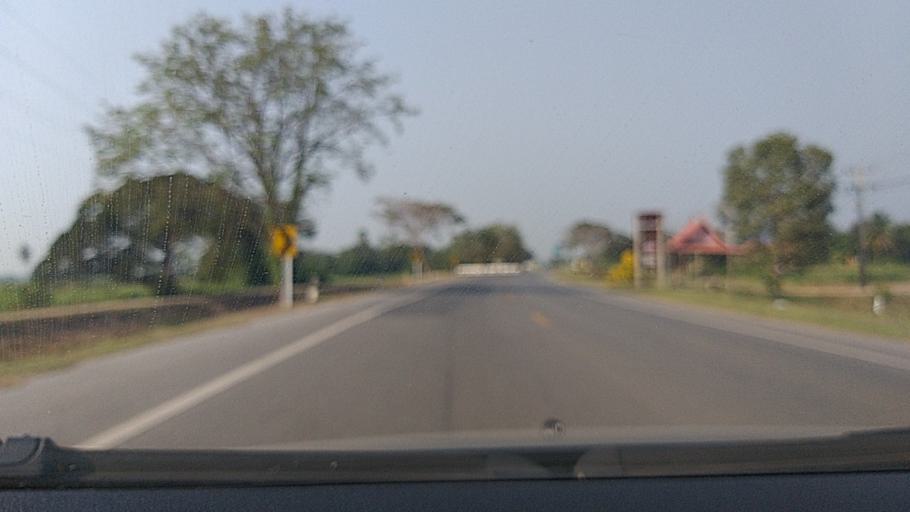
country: TH
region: Sing Buri
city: Tha Chang
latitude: 14.7249
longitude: 100.4300
